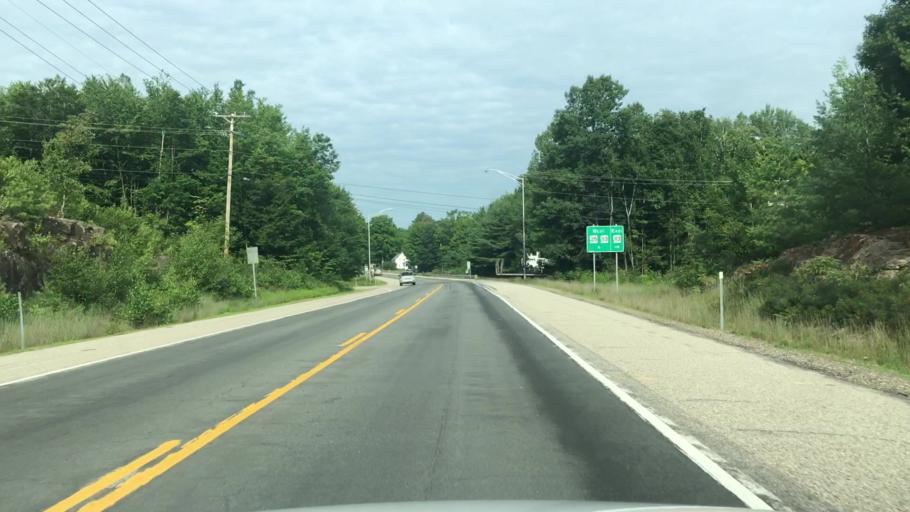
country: US
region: New Hampshire
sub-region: Carroll County
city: Tamworth
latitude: 43.8301
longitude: -71.2718
